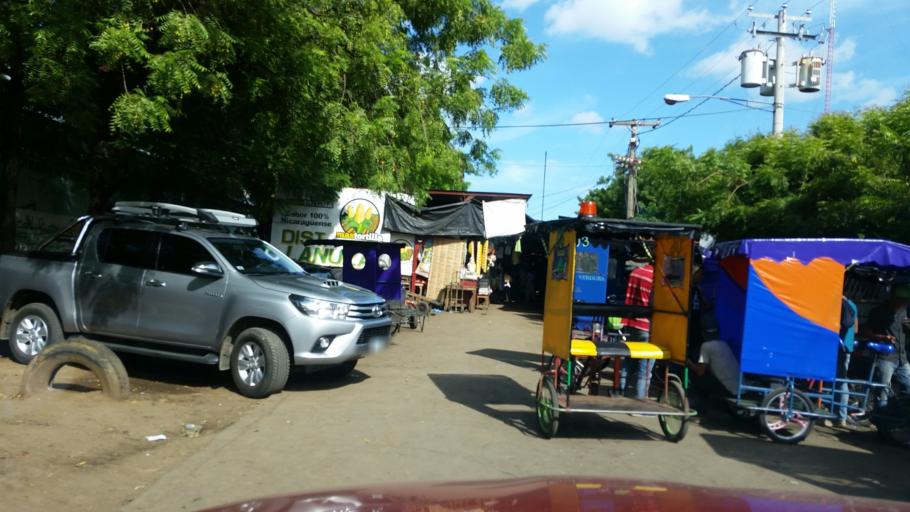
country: NI
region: Managua
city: Managua
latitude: 12.1256
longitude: -86.2446
